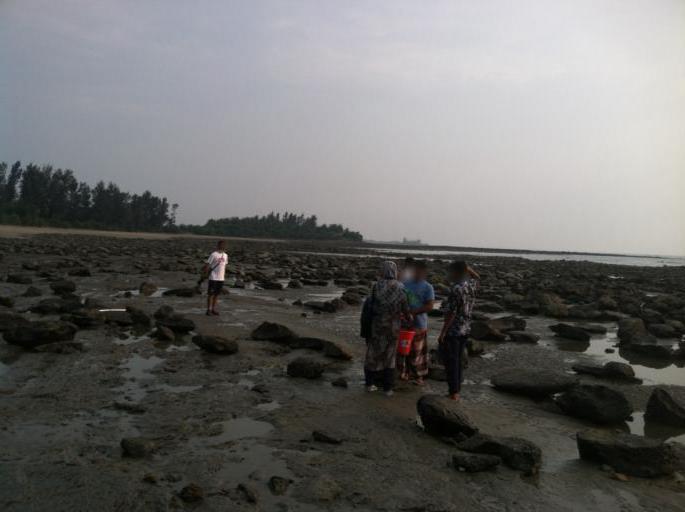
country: BD
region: Chittagong
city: Teknaf
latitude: 20.6186
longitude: 92.3241
